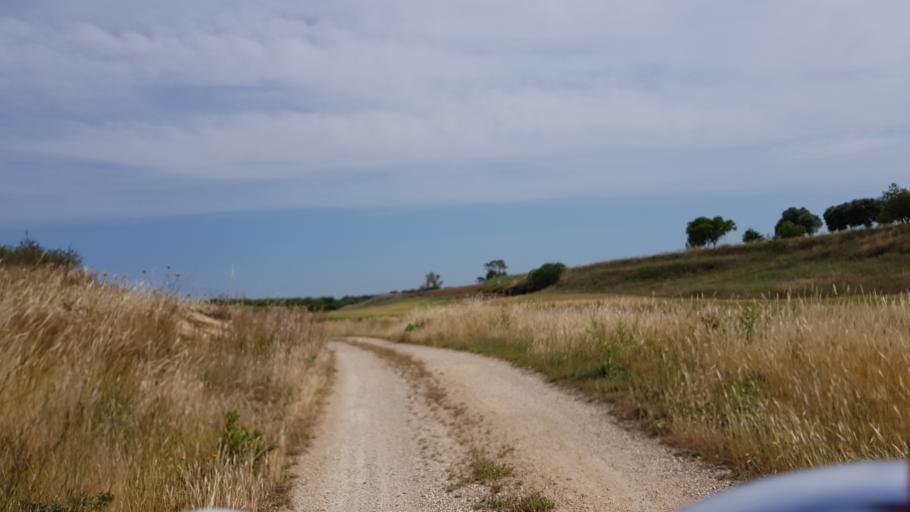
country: IT
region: Apulia
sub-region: Provincia di Brindisi
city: San Vito dei Normanni
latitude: 40.6642
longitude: 17.7974
